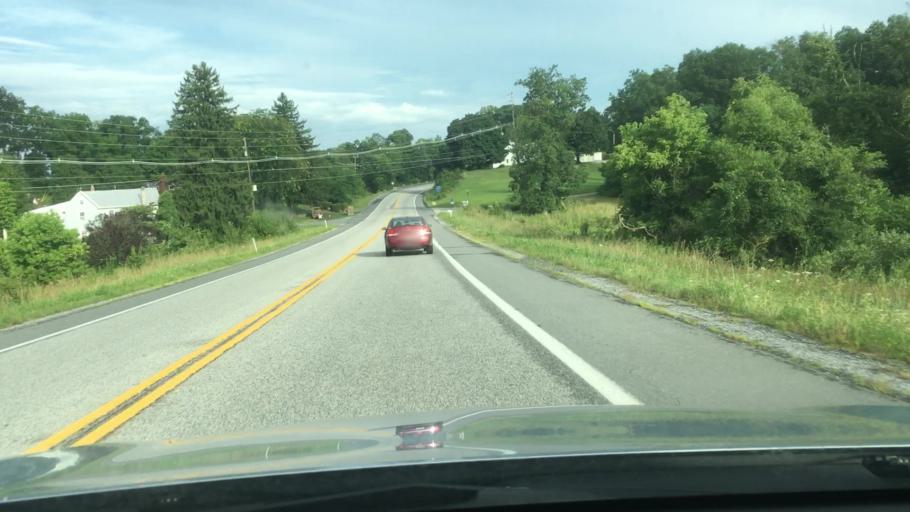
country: US
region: Pennsylvania
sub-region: York County
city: Dillsburg
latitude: 40.0787
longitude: -76.9295
